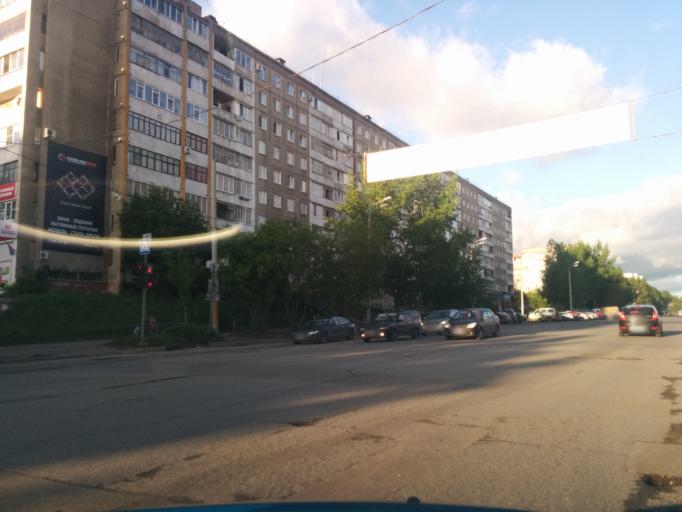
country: RU
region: Perm
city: Kondratovo
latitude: 57.9980
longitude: 56.1673
